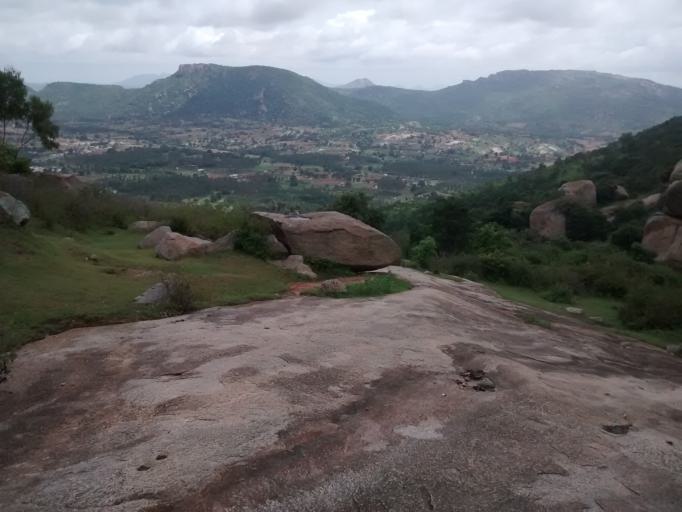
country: IN
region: Karnataka
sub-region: Tumkur
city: Tumkur
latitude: 13.3771
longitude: 77.2086
